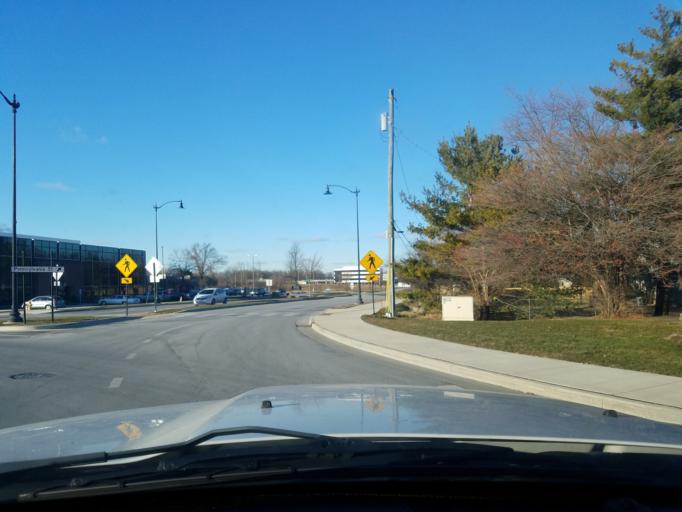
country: US
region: Indiana
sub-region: Hamilton County
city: Carmel
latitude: 39.9424
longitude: -86.1555
